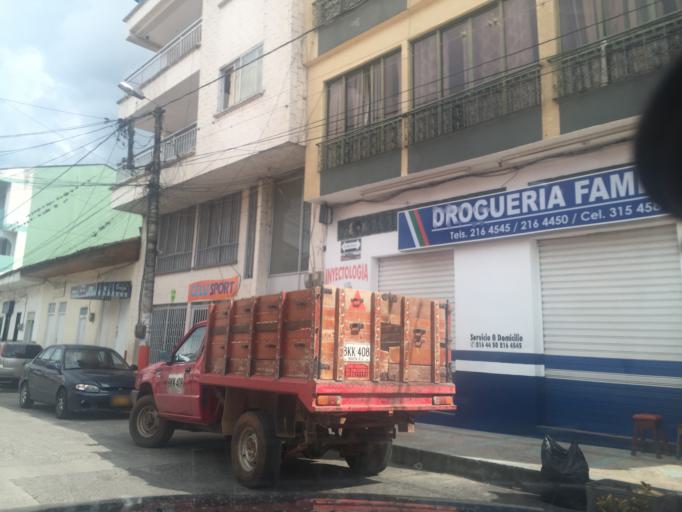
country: CO
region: Valle del Cauca
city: Caicedonia
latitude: 4.3329
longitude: -75.8297
